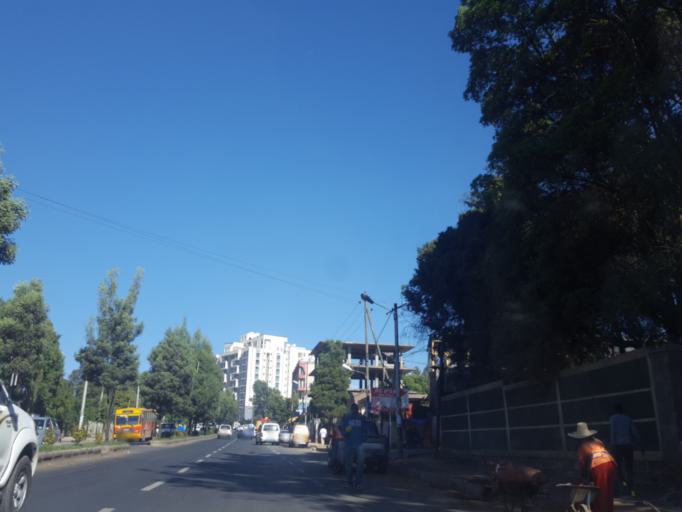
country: ET
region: Adis Abeba
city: Addis Ababa
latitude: 9.0556
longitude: 38.7413
